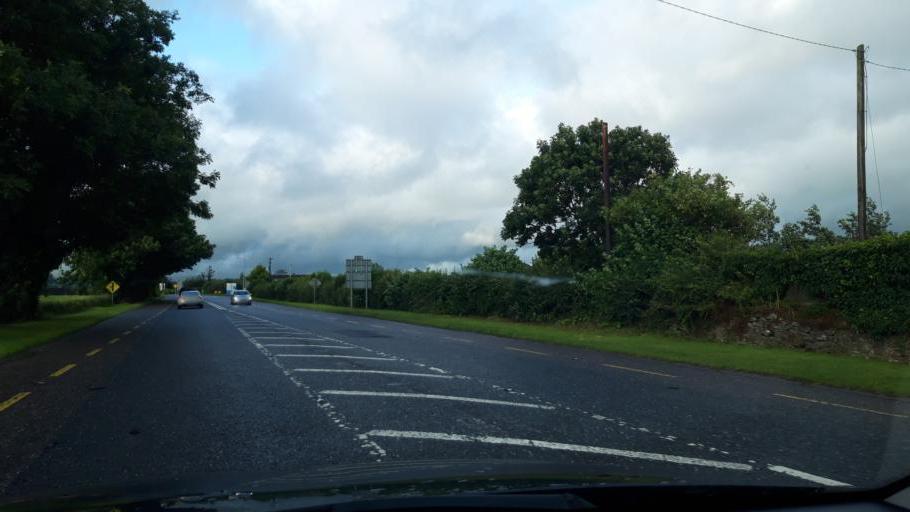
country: IE
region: Munster
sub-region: County Cork
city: Fermoy
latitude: 52.1601
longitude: -8.2709
